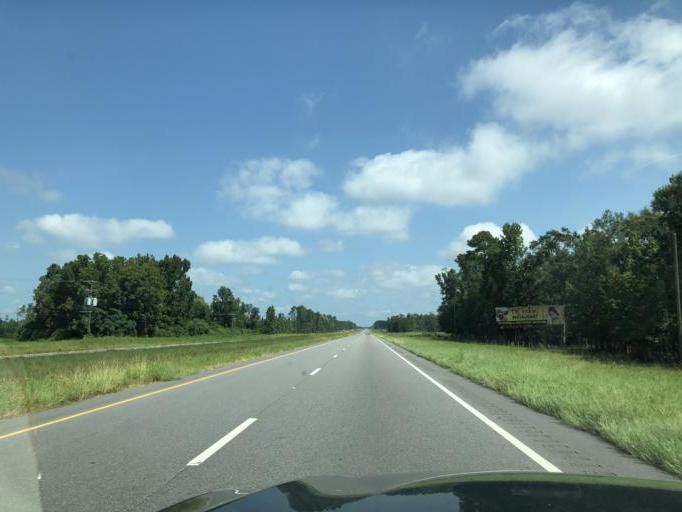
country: US
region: Alabama
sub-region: Houston County
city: Cottonwood
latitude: 31.0239
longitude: -85.4071
